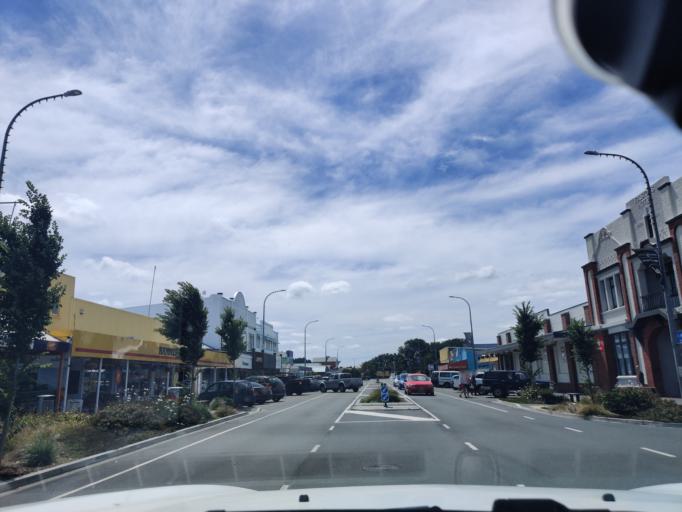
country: NZ
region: Manawatu-Wanganui
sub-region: Horowhenua District
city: Foxton
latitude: -40.4728
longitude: 175.2817
